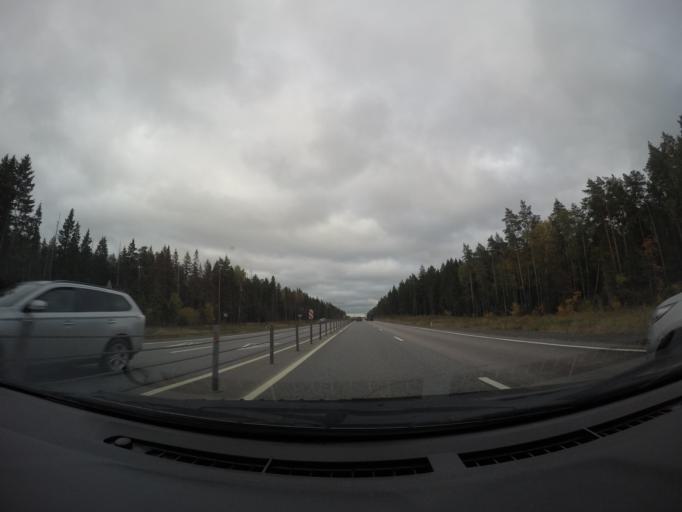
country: RU
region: Moskovskaya
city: Tuchkovo
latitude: 55.5534
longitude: 36.5124
